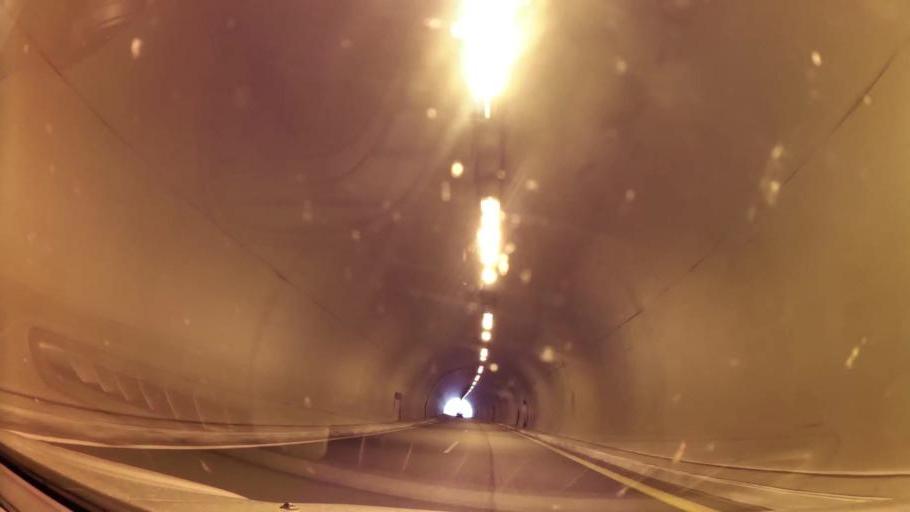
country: GR
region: Central Macedonia
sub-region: Nomos Imathias
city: Rizomata
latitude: 40.4323
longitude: 22.1826
